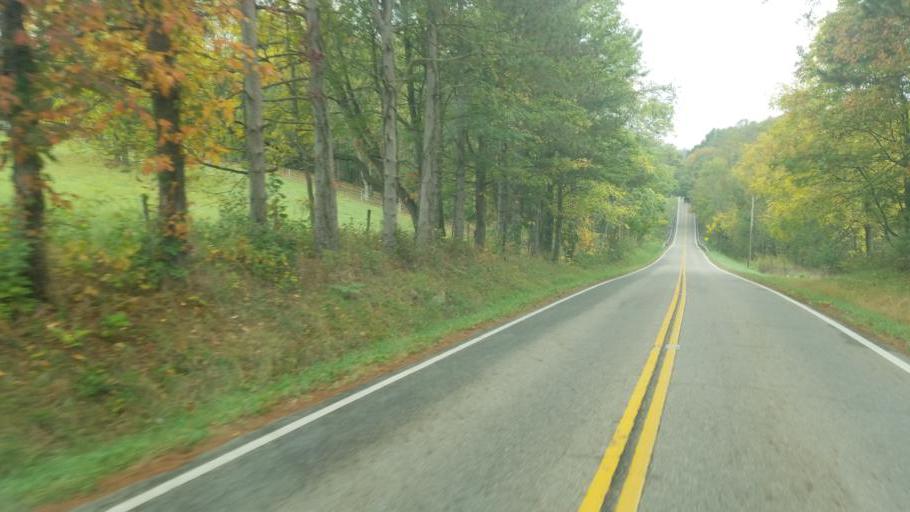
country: US
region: Ohio
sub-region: Carroll County
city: Lake Mohawk
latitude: 40.6049
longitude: -81.2699
